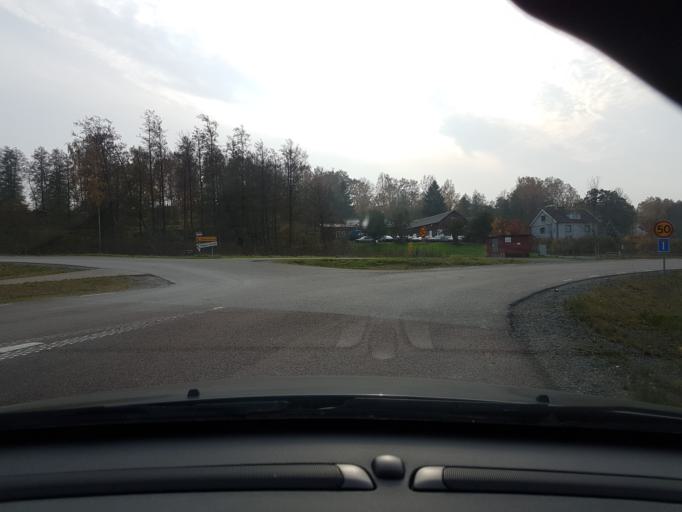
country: SE
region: Vaestra Goetaland
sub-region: Ale Kommun
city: Alvangen
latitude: 57.9663
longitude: 12.1510
